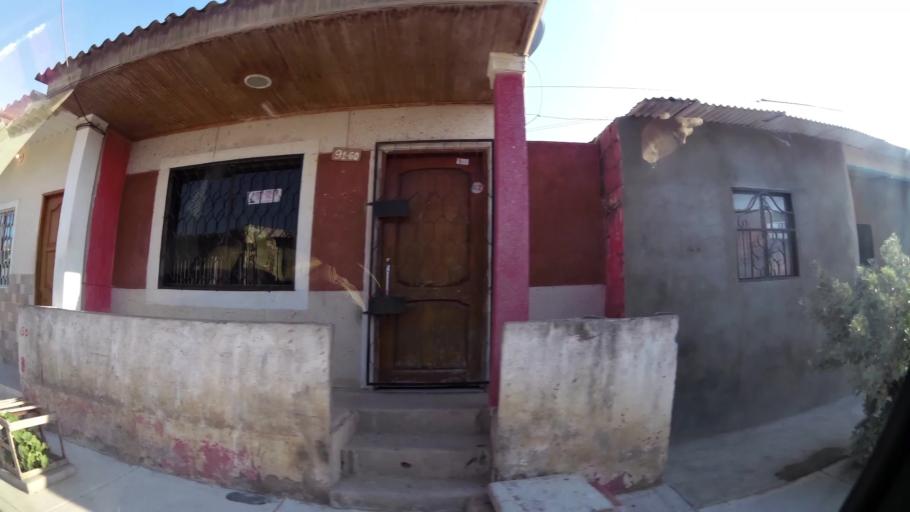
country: CO
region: Atlantico
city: Barranquilla
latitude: 11.0430
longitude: -74.8289
